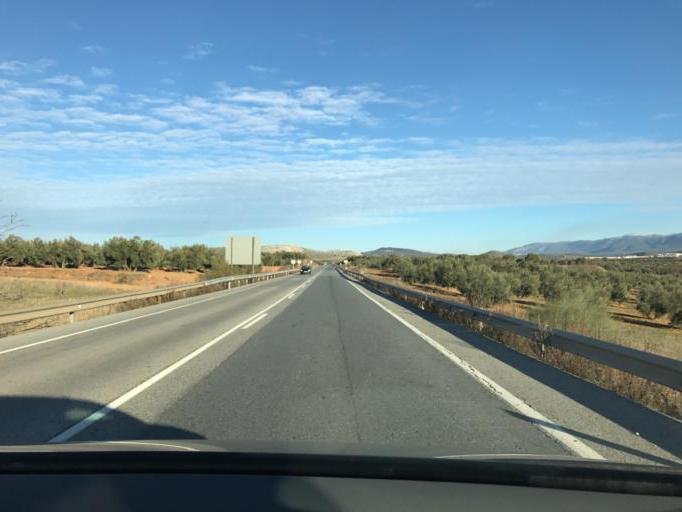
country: ES
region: Andalusia
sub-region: Provincia de Granada
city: Iznalloz
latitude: 37.4000
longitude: -3.5471
